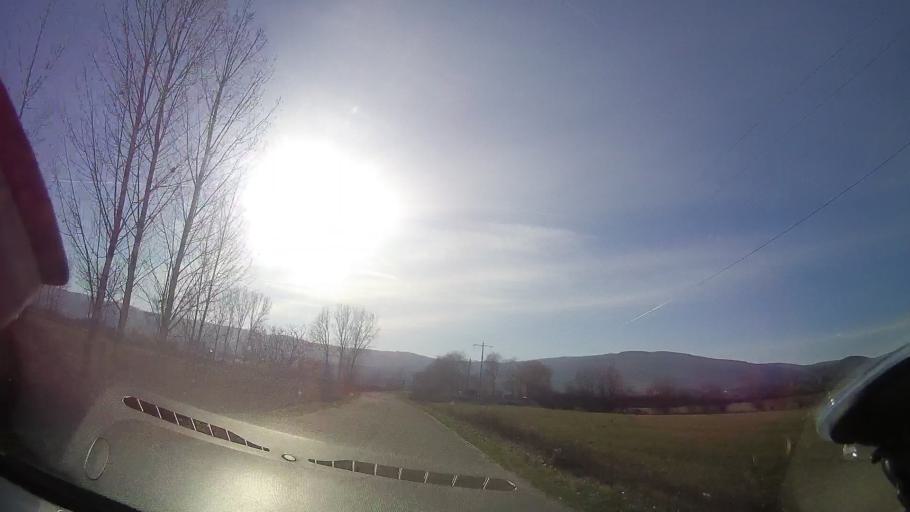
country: RO
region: Bihor
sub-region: Comuna Magesti
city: Magesti
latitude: 47.0142
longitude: 22.4575
